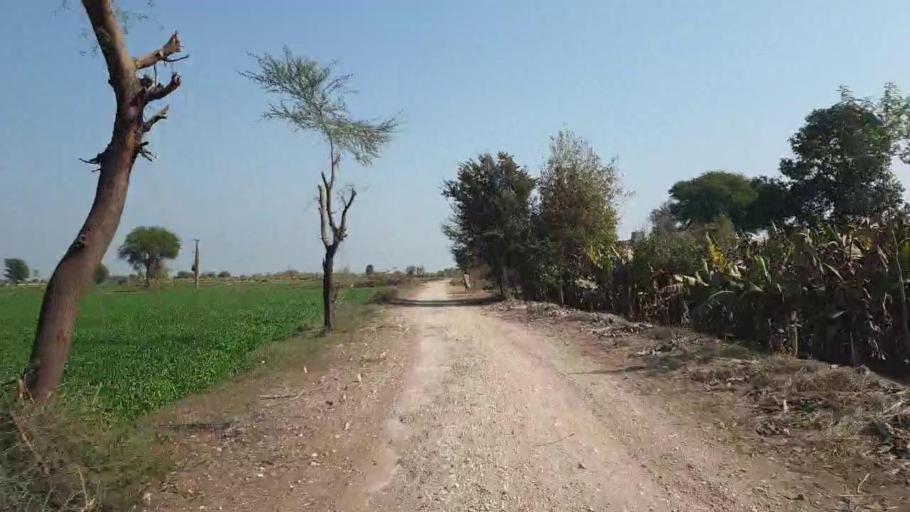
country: PK
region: Sindh
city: Shahdadpur
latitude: 25.9453
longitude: 68.4911
